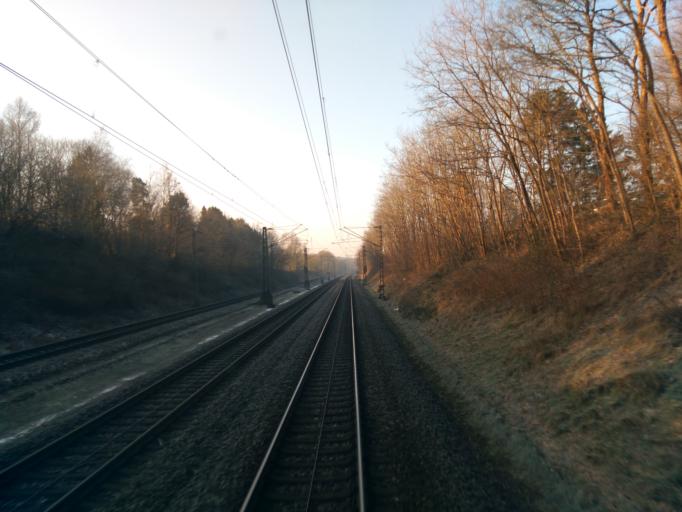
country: DE
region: Lower Saxony
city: Buchholz in der Nordheide
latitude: 53.3138
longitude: 9.8202
